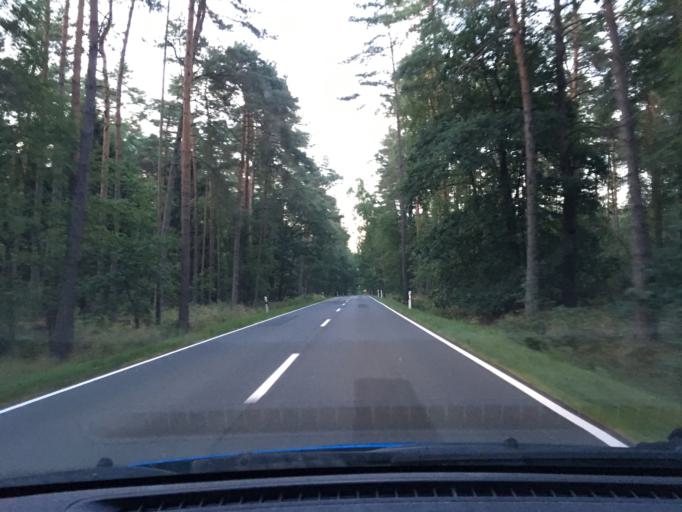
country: DE
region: Lower Saxony
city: Dahlenburg
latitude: 53.1569
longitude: 10.6833
